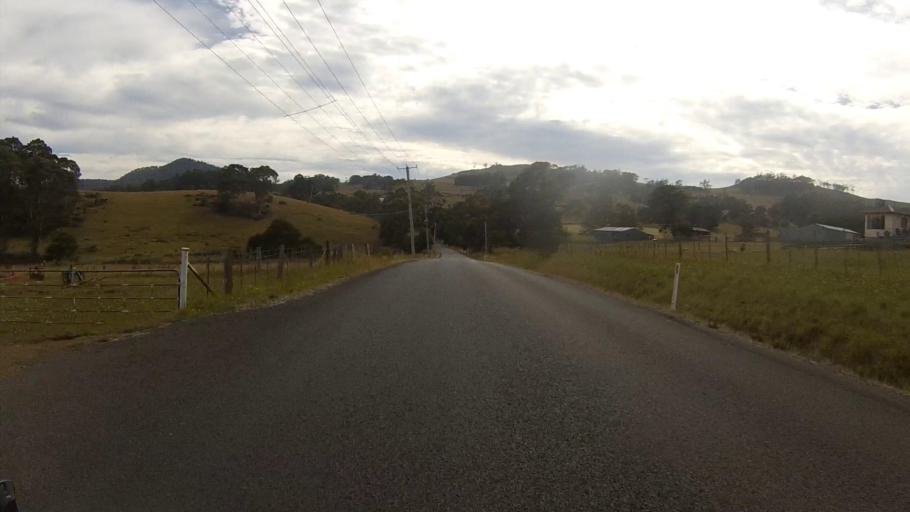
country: AU
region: Tasmania
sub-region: Sorell
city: Sorell
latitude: -42.7893
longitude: 147.8036
